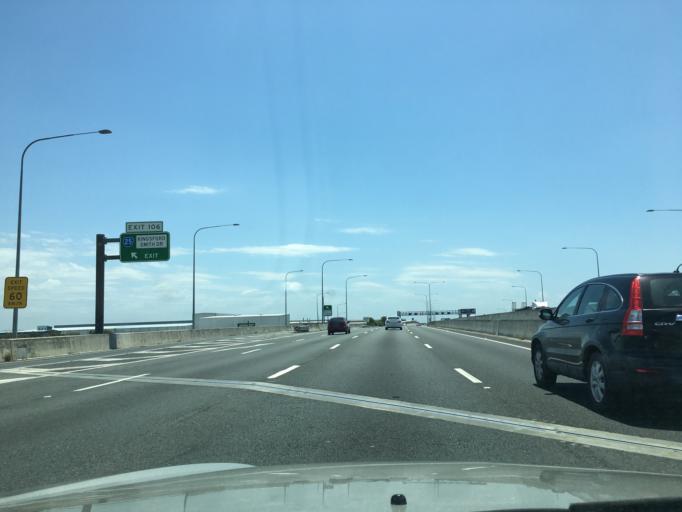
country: AU
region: Queensland
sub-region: Brisbane
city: Ascot
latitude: -27.4341
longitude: 153.0948
